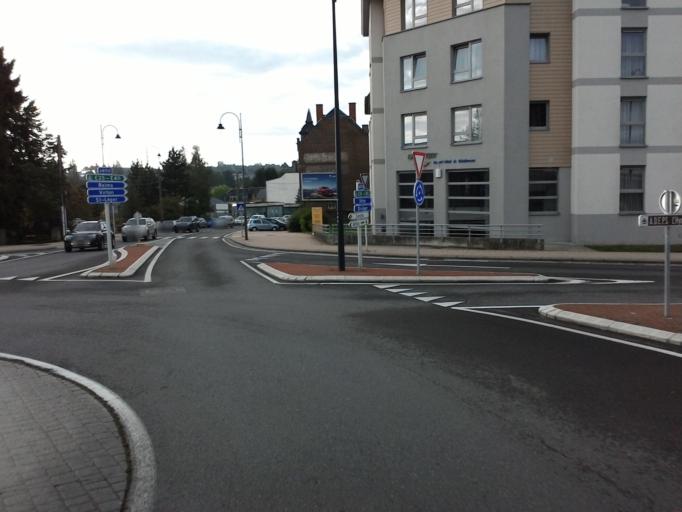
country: BE
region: Wallonia
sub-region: Province du Luxembourg
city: Arlon
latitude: 49.6804
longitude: 5.8054
